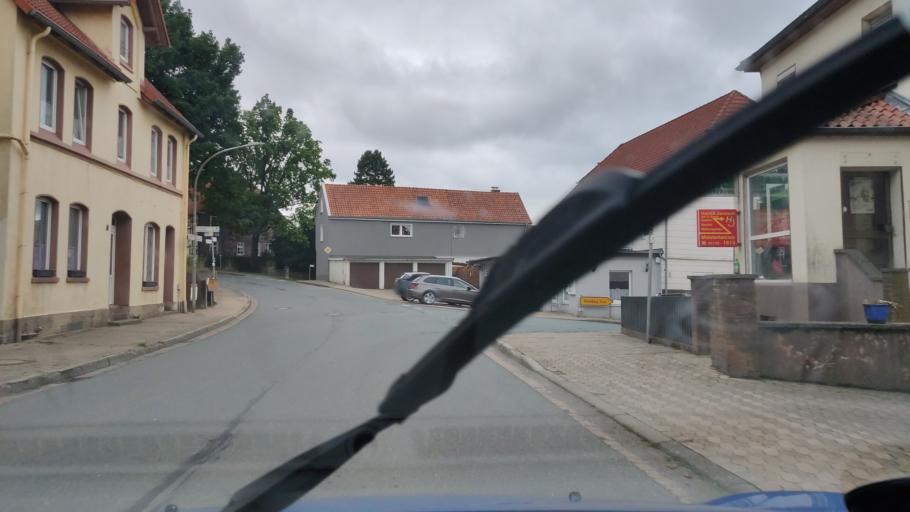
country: DE
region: Lower Saxony
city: Coppenbrugge
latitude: 52.0862
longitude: 9.4998
